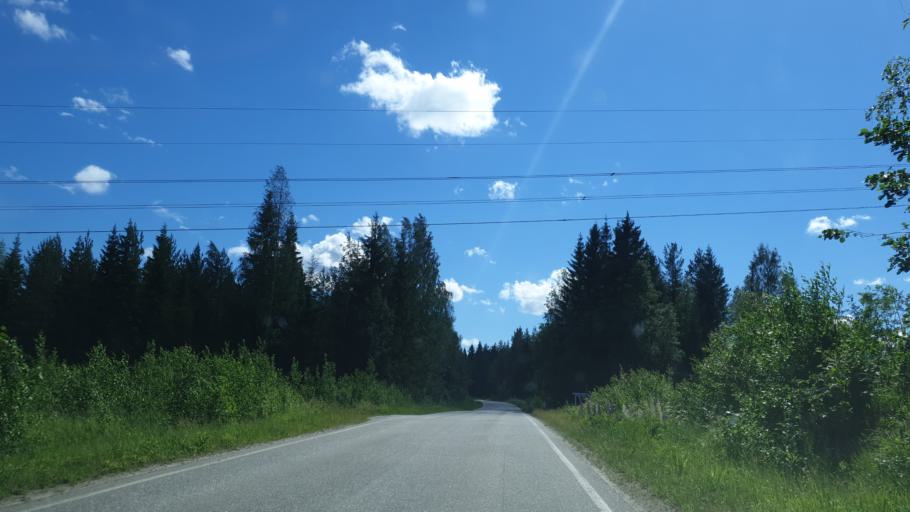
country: FI
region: Northern Savo
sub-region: Koillis-Savo
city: Kaavi
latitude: 63.0025
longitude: 28.5018
